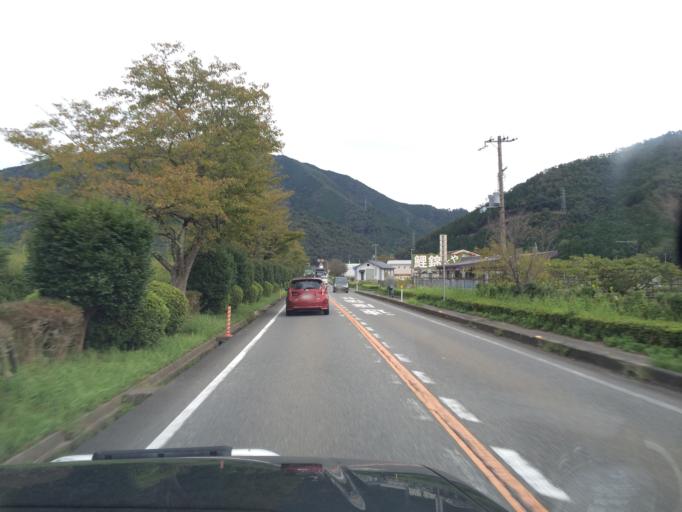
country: JP
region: Hyogo
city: Toyooka
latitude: 35.3791
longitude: 134.8143
